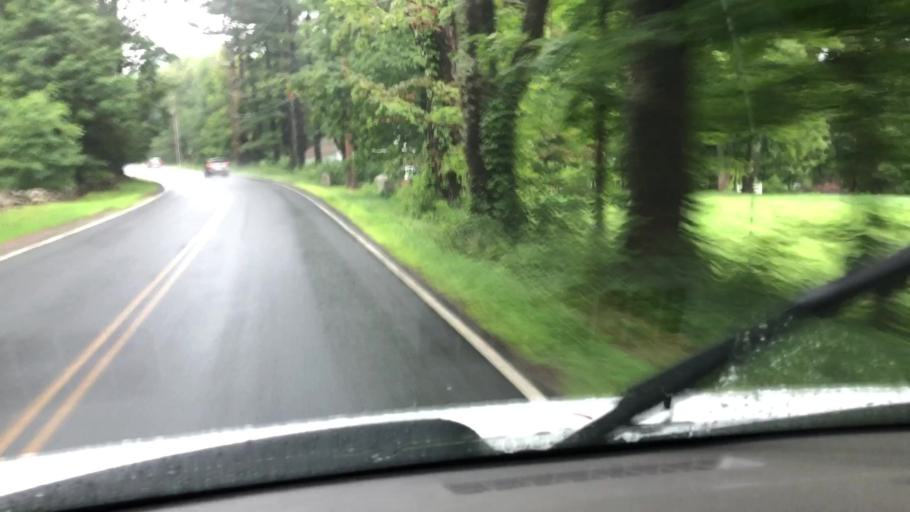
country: US
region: Massachusetts
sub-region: Hampshire County
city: Chesterfield
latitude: 42.4205
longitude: -72.9420
